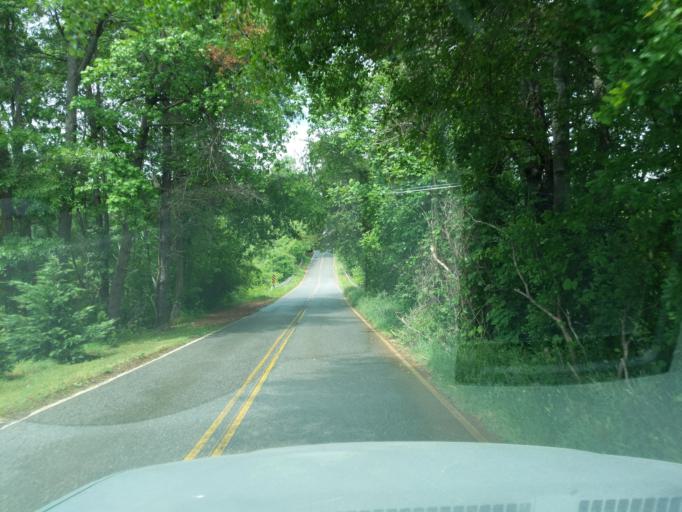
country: US
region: South Carolina
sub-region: Spartanburg County
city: Inman Mills
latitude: 35.0059
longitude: -82.1178
